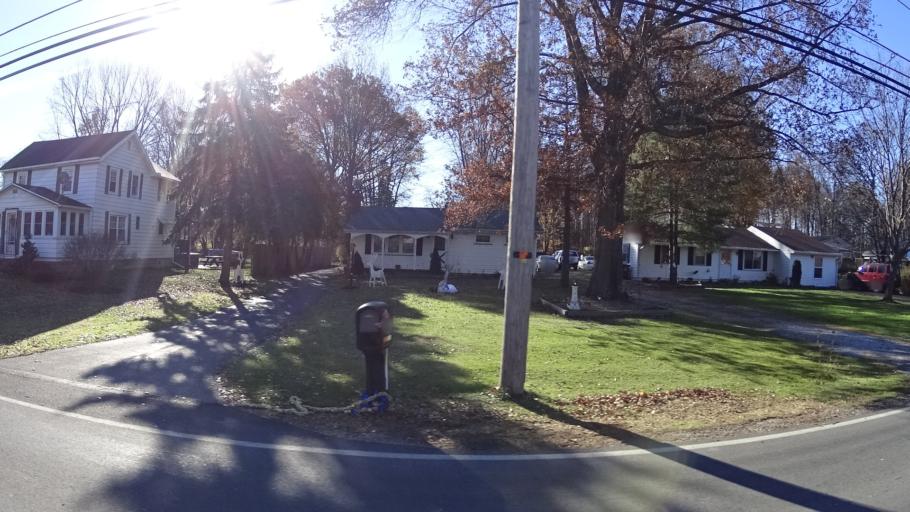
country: US
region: Ohio
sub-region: Lorain County
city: Elyria
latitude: 41.4002
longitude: -82.1402
